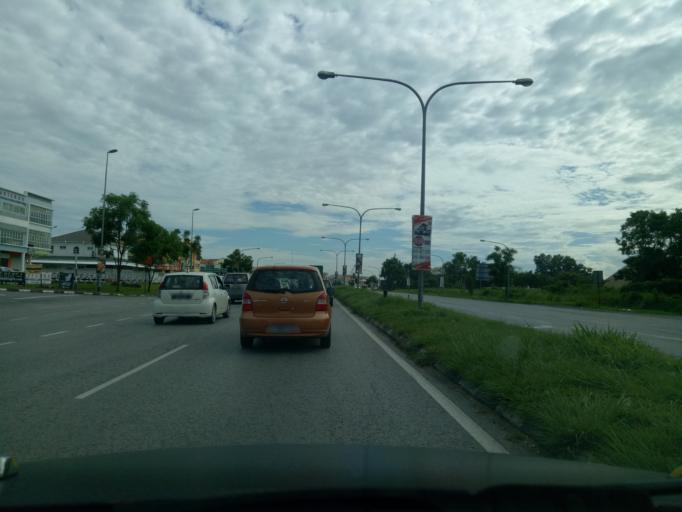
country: MY
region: Sarawak
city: Kuching
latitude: 1.4711
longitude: 110.3285
